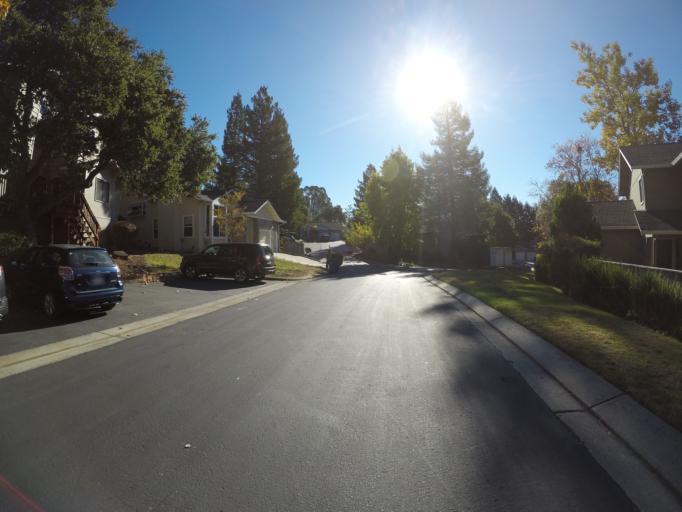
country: US
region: California
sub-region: Santa Cruz County
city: Scotts Valley
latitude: 37.0504
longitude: -122.0241
